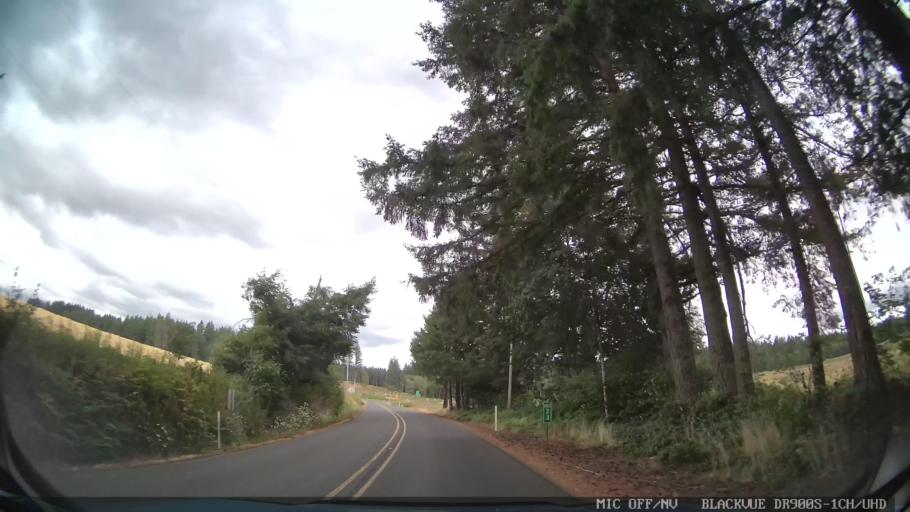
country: US
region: Oregon
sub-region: Linn County
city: Lyons
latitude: 44.8481
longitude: -122.6682
